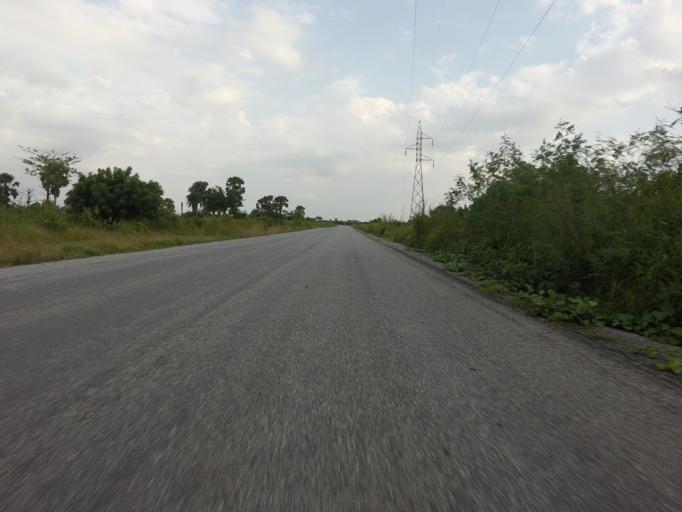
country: GH
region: Volta
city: Ho
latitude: 6.3896
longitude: 0.5272
